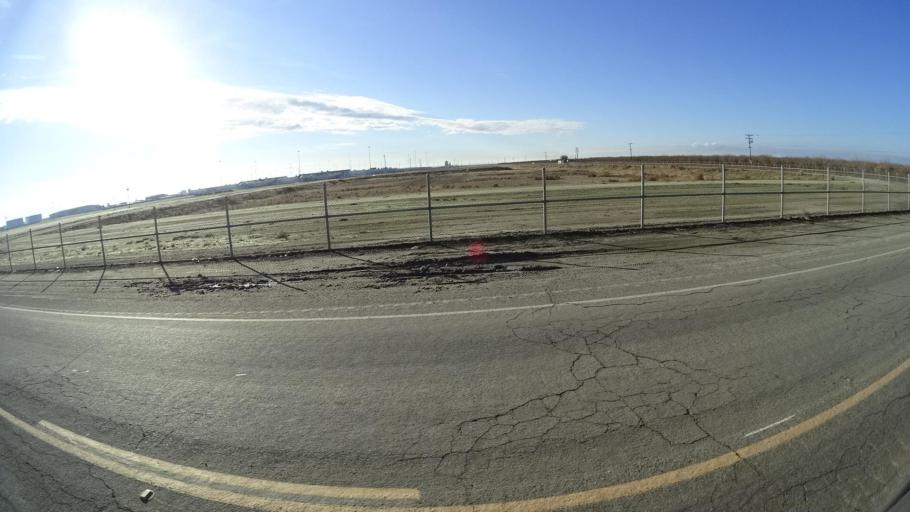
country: US
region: California
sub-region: Kern County
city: Delano
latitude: 35.7758
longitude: -119.3289
